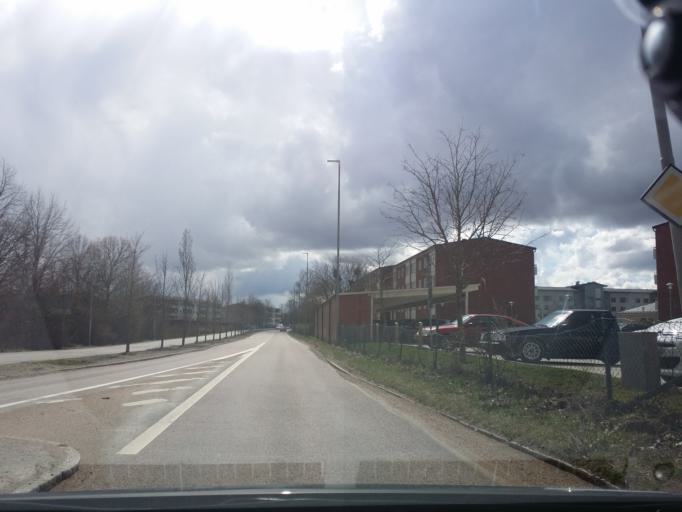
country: SE
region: Vaestmanland
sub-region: Sala Kommun
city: Sala
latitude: 59.9261
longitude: 16.5900
